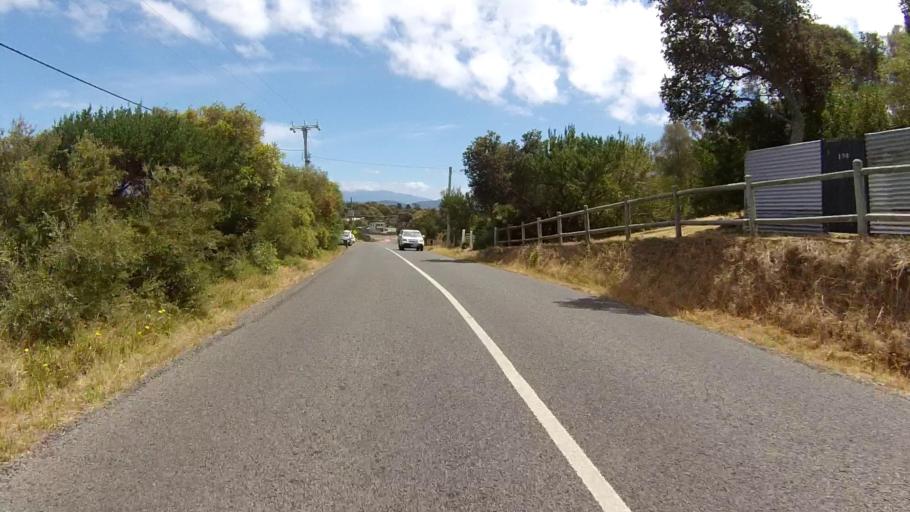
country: AU
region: Tasmania
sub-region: Sorell
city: Sorell
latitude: -42.8667
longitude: 147.6162
